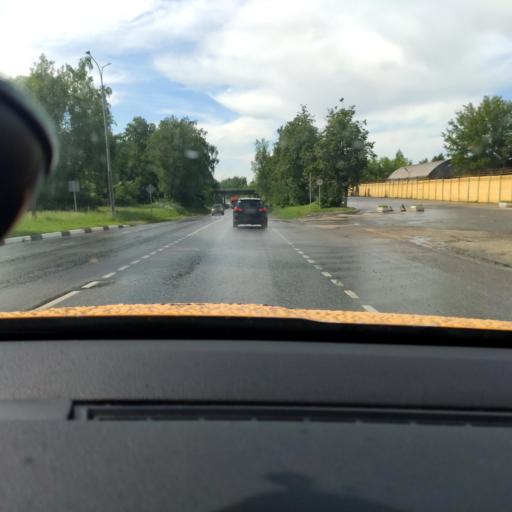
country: RU
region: Moskovskaya
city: Stupino
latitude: 54.9179
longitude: 38.0617
